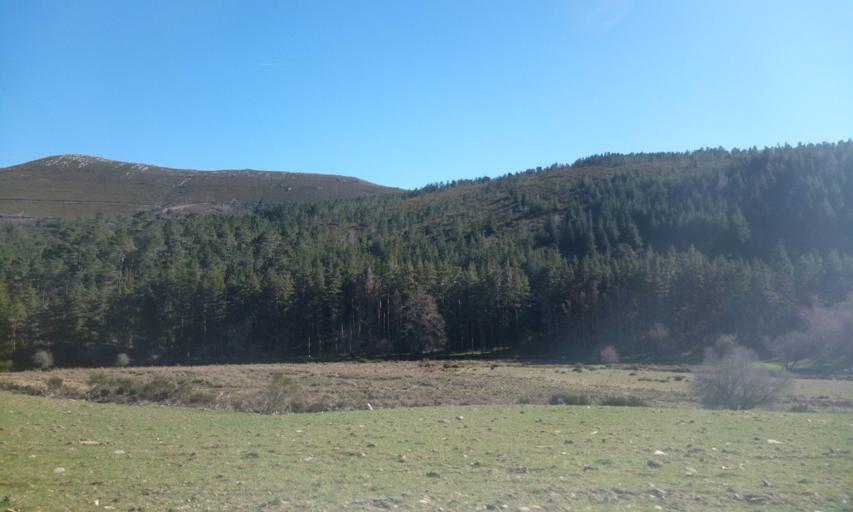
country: PT
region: Guarda
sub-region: Manteigas
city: Manteigas
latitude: 40.4443
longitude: -7.5134
